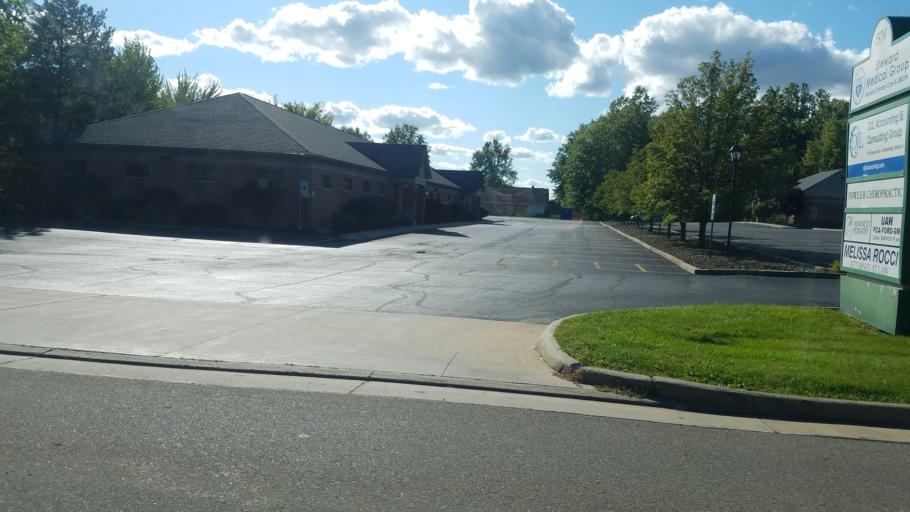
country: US
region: Ohio
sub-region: Mahoning County
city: Austintown
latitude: 41.0858
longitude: -80.7629
